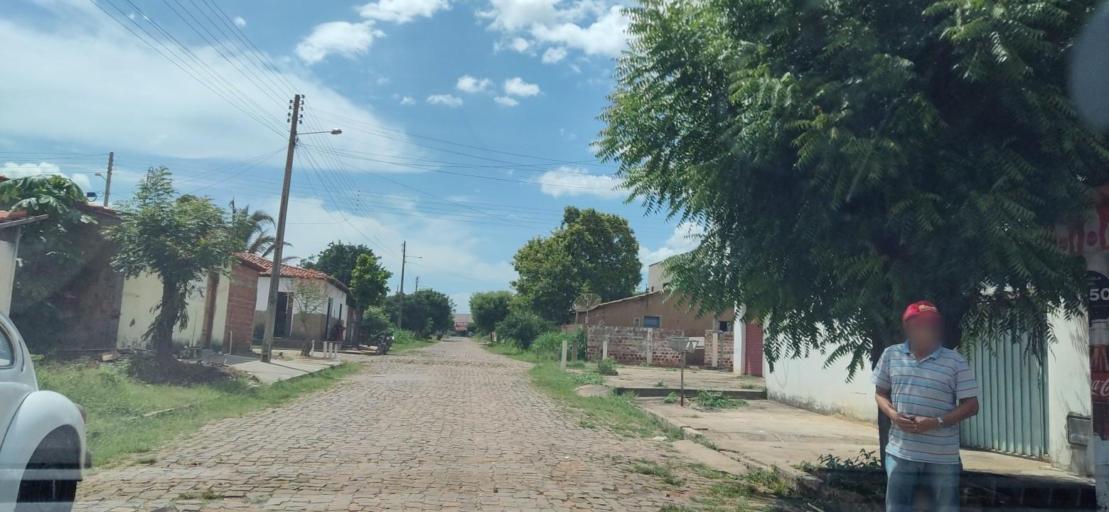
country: BR
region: Piaui
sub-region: Valenca Do Piaui
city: Valenca do Piaui
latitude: -6.4101
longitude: -41.7435
